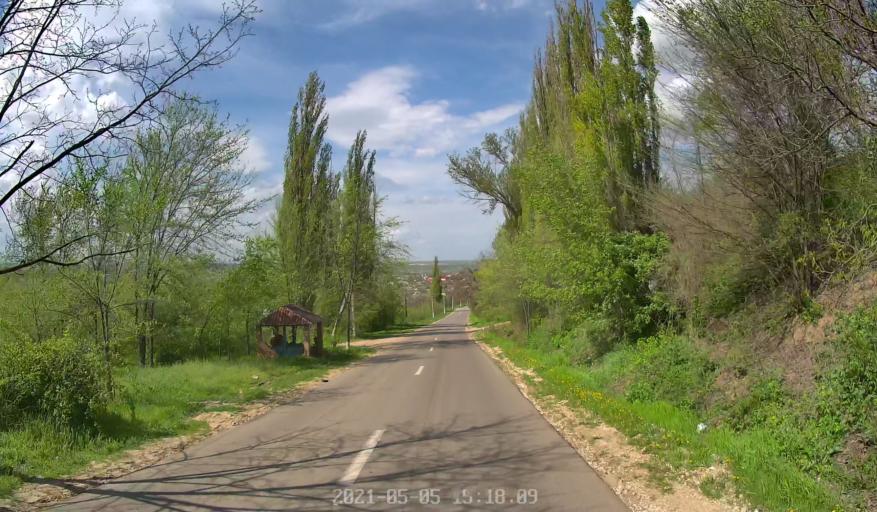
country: MD
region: Criuleni
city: Criuleni
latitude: 47.1174
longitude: 29.1943
